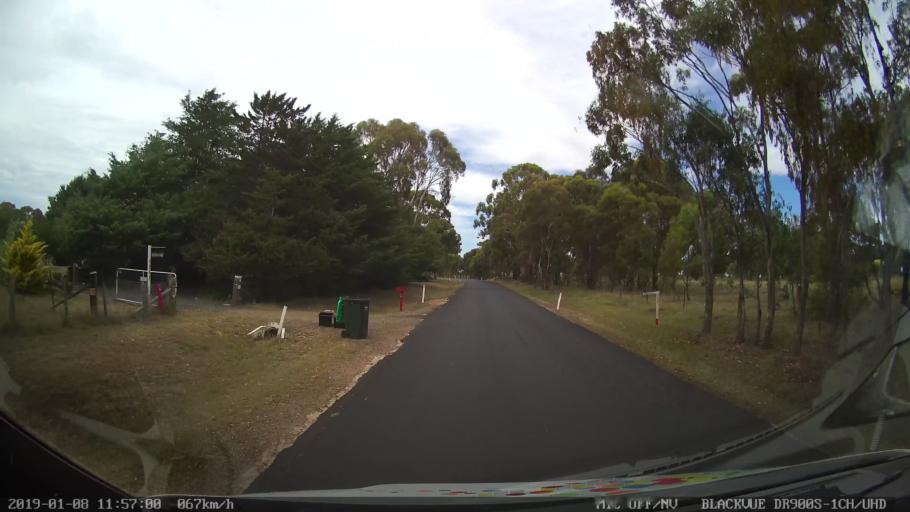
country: AU
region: New South Wales
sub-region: Armidale Dumaresq
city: Armidale
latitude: -30.4461
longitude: 151.5652
